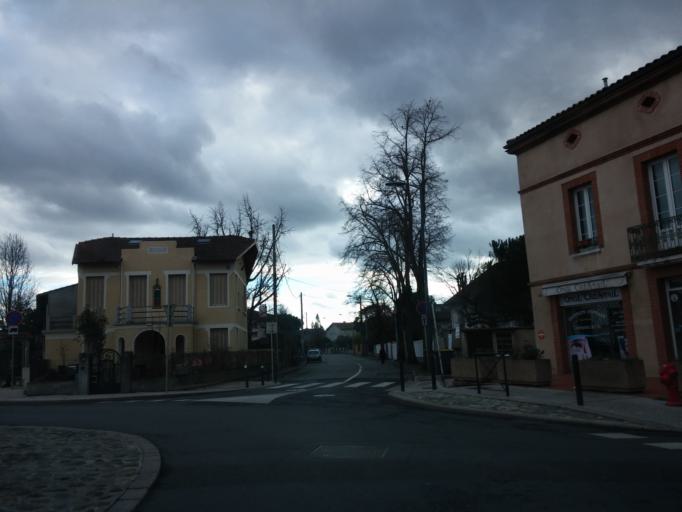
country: FR
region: Midi-Pyrenees
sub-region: Departement de la Haute-Garonne
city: Blagnac
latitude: 43.6312
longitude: 1.3973
